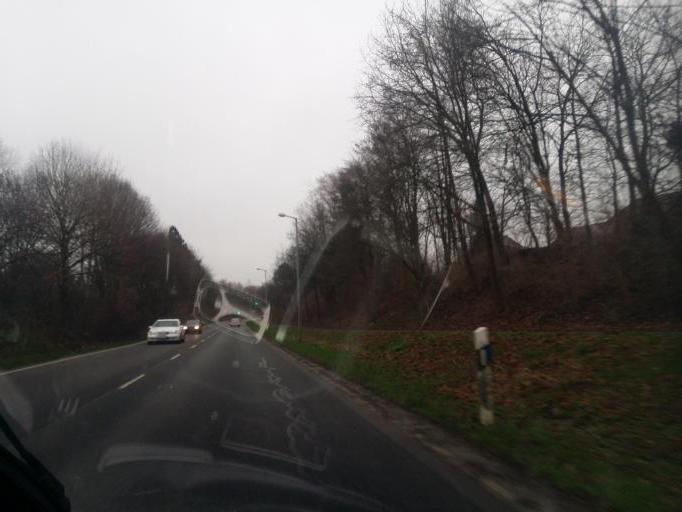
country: DE
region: Schleswig-Holstein
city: Heide
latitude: 54.2030
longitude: 9.1194
